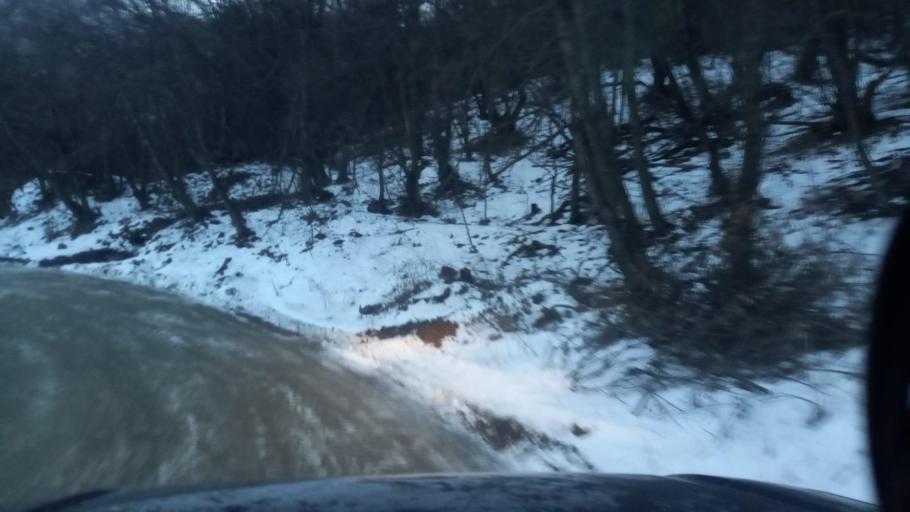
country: RU
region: Ingushetiya
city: Dzhayrakh
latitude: 42.8284
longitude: 44.5847
